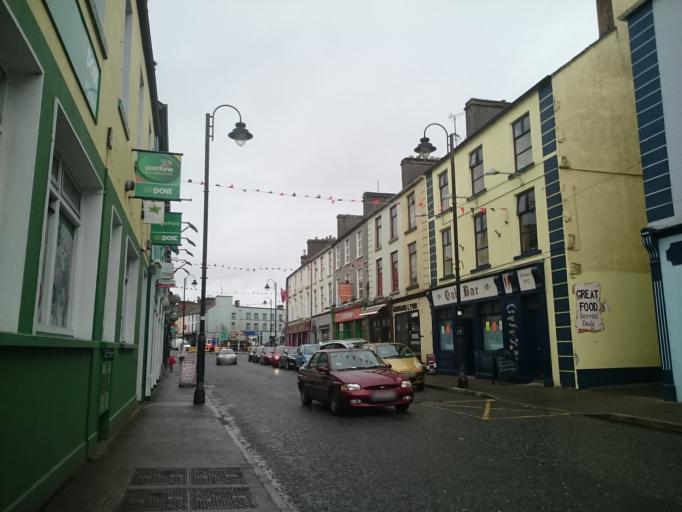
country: IE
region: Connaught
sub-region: Maigh Eo
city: Ballyhaunis
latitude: 53.7625
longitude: -8.7643
